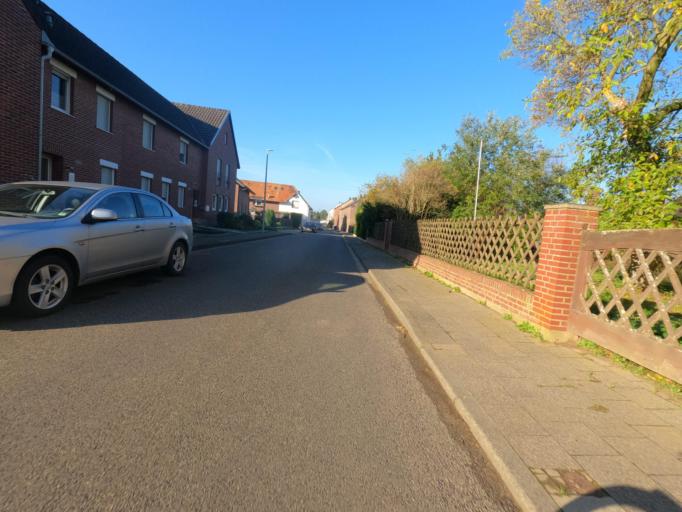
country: DE
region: North Rhine-Westphalia
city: Erkelenz
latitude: 51.0820
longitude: 6.3483
